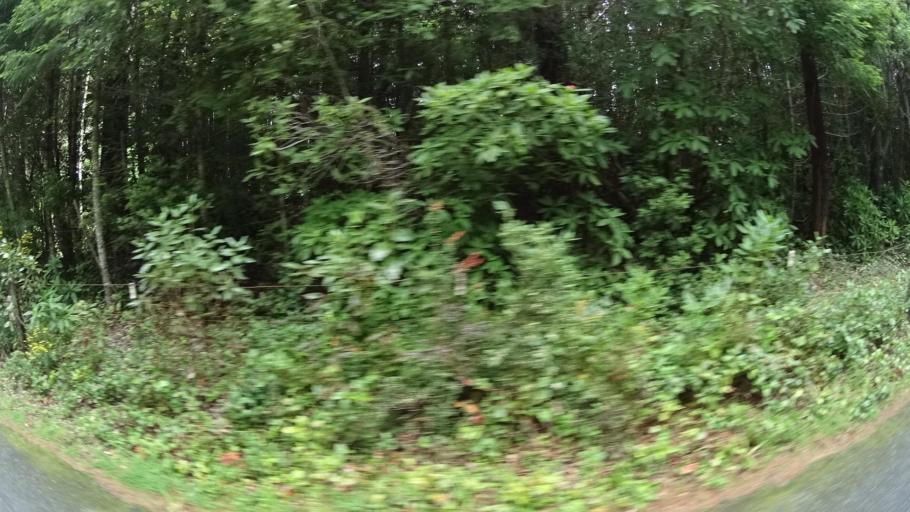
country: US
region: California
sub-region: Humboldt County
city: Blue Lake
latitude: 40.8060
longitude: -123.9885
